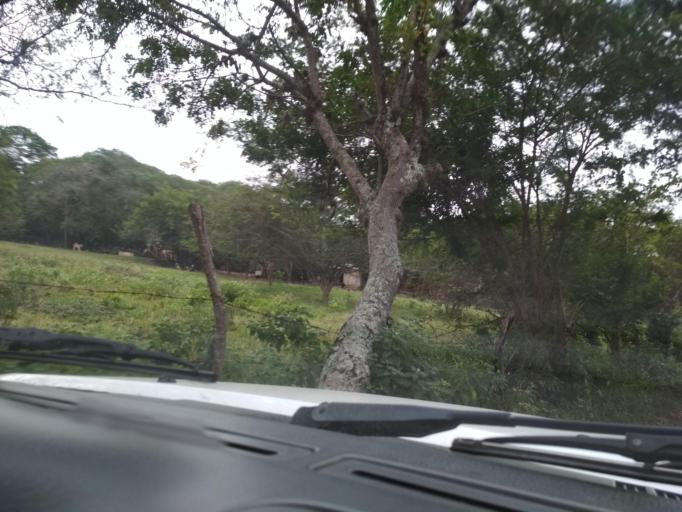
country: MX
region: Veracruz
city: El Castillo
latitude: 19.5832
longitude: -96.8383
